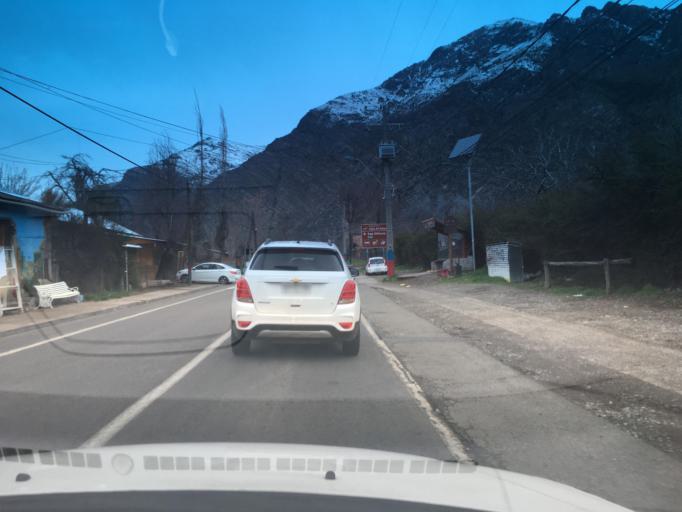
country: CL
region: Santiago Metropolitan
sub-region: Provincia de Cordillera
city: Puente Alto
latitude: -33.7158
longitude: -70.3314
